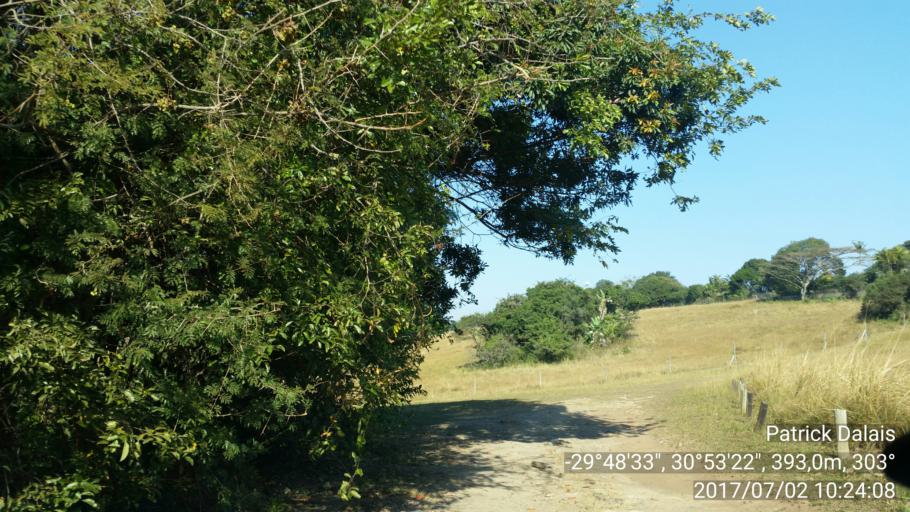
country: ZA
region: KwaZulu-Natal
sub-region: eThekwini Metropolitan Municipality
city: Berea
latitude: -29.8093
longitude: 30.8895
